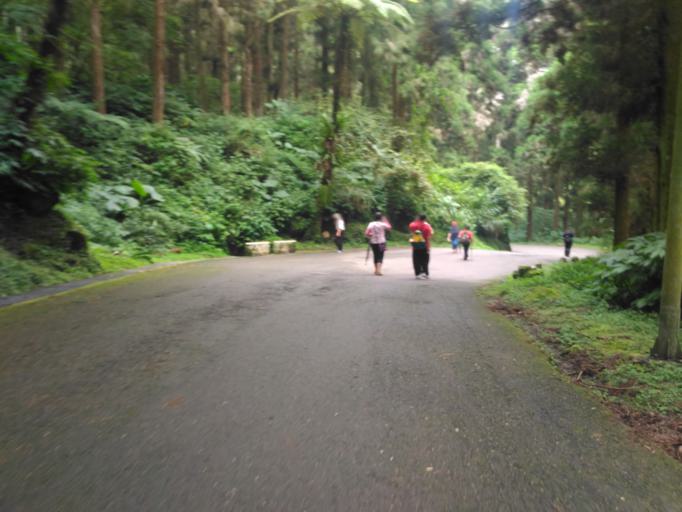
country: TW
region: Taiwan
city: Lugu
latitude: 23.6620
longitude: 120.7956
